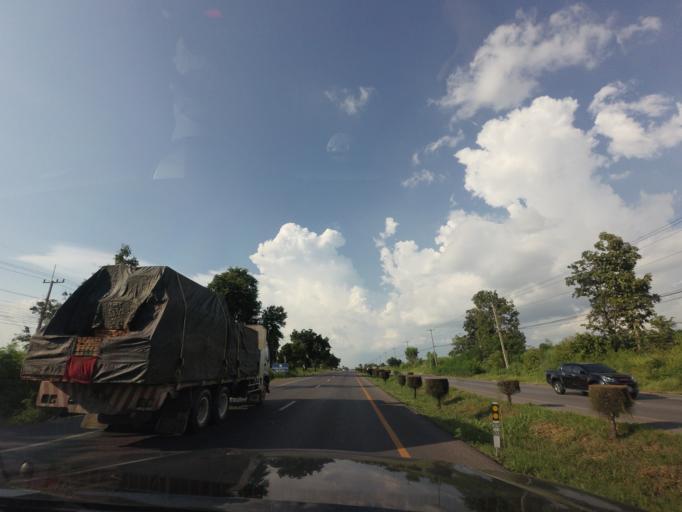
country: TH
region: Khon Kaen
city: Ban Haet
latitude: 16.1614
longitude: 102.7537
